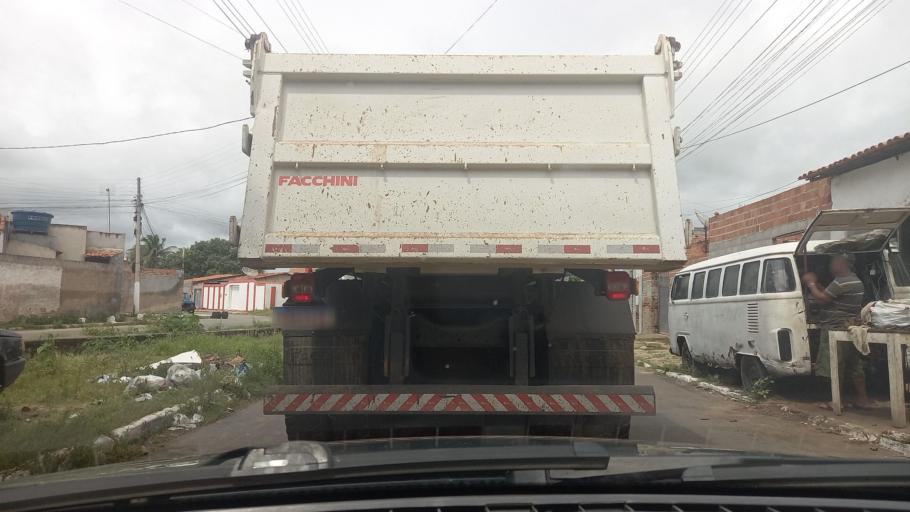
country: BR
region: Alagoas
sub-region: Delmiro Gouveia
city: Delmiro Gouveia
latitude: -9.3842
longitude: -38.0028
